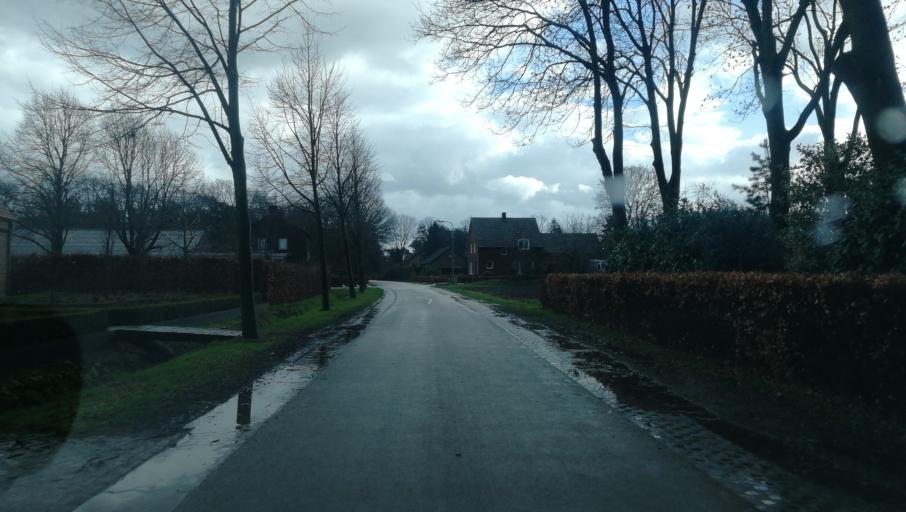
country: NL
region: Limburg
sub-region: Gemeente Peel en Maas
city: Maasbree
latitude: 51.3517
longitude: 6.0538
